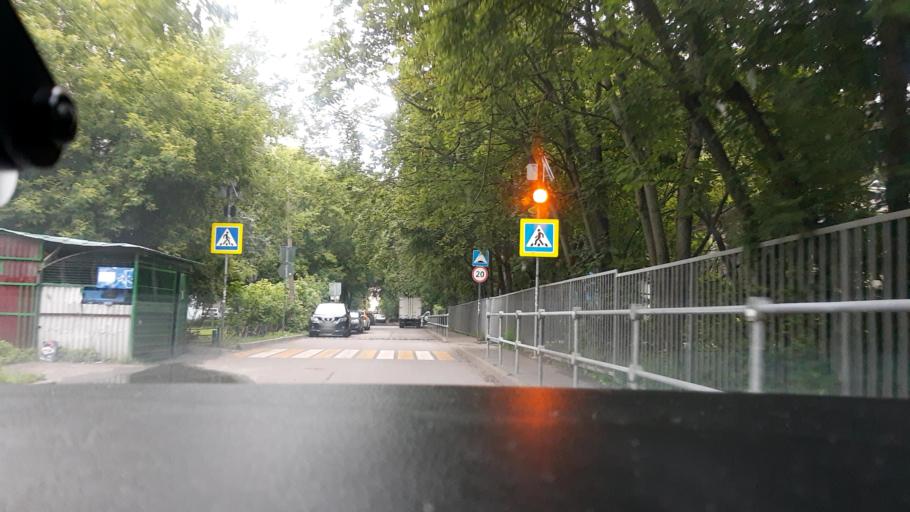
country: RU
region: Moskovskaya
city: Dolgoprudnyy
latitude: 55.9479
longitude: 37.5106
